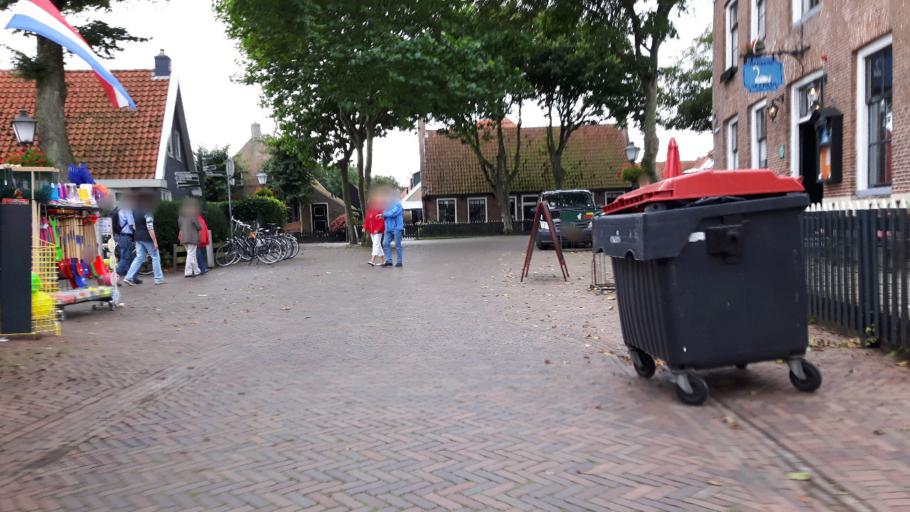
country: NL
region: Friesland
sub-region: Gemeente Ameland
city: Hollum
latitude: 53.4412
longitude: 5.6383
